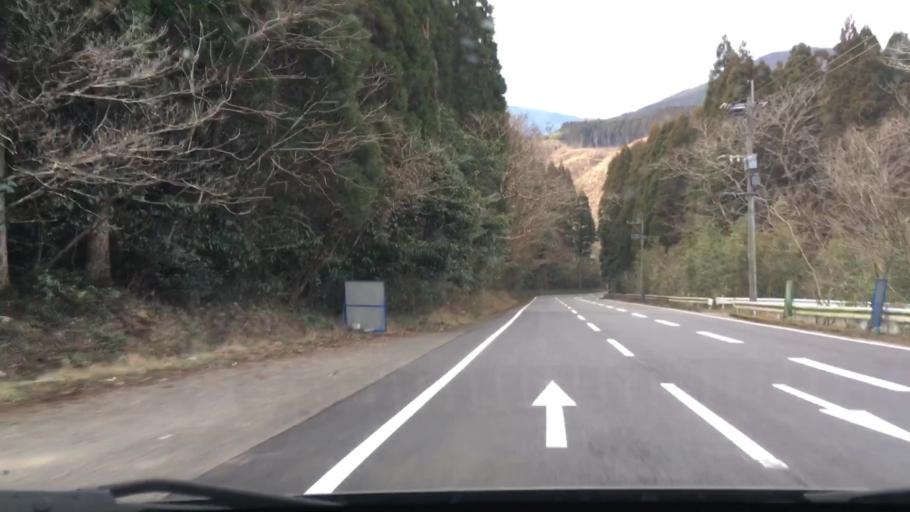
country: JP
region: Miyazaki
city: Nichinan
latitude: 31.7064
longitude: 131.3293
